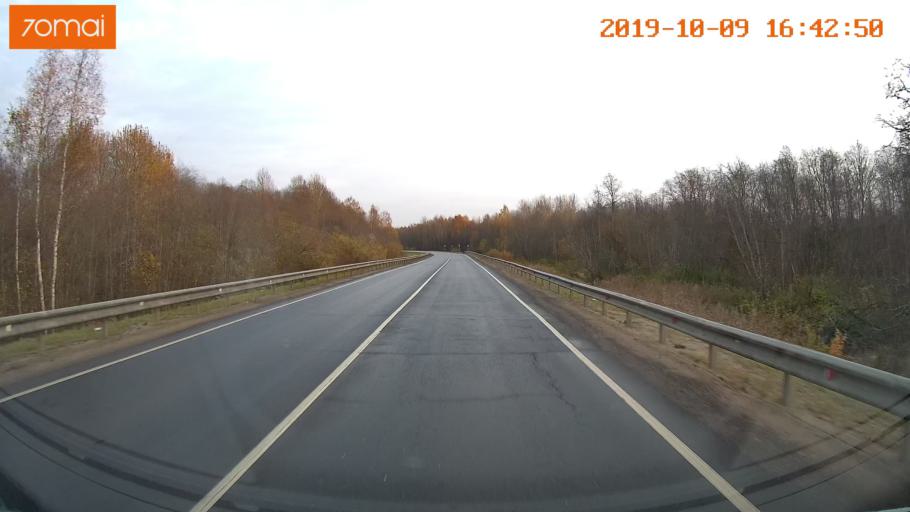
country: RU
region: Kostroma
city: Volgorechensk
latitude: 57.4580
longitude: 41.1087
